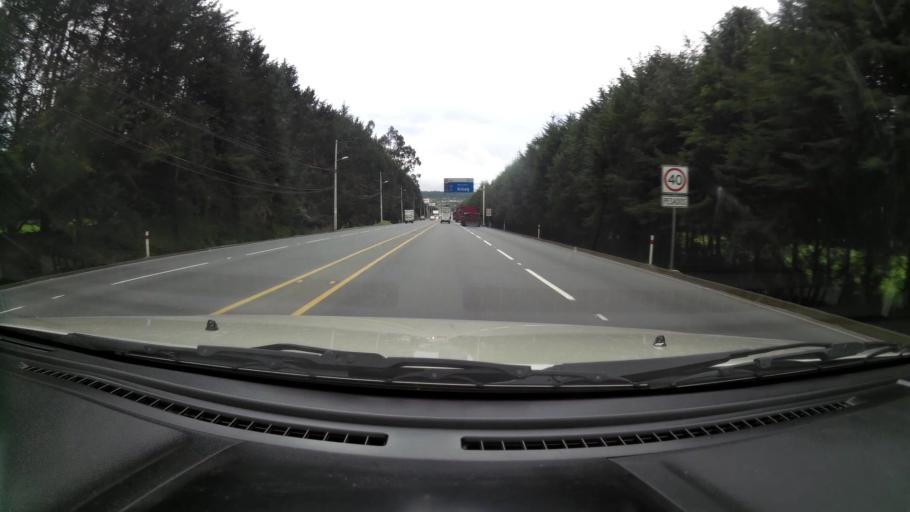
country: EC
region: Pichincha
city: Machachi
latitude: -0.4665
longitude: -78.5914
